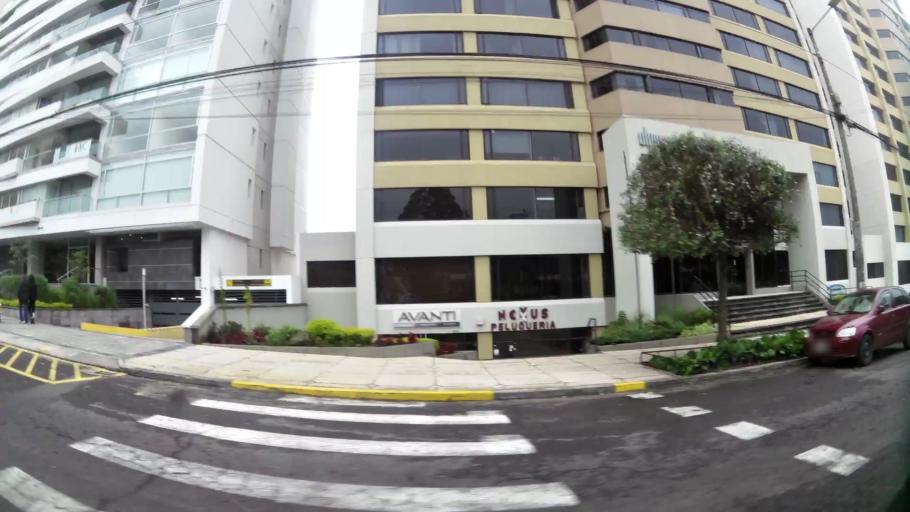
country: EC
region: Pichincha
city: Quito
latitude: -0.1990
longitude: -78.4795
